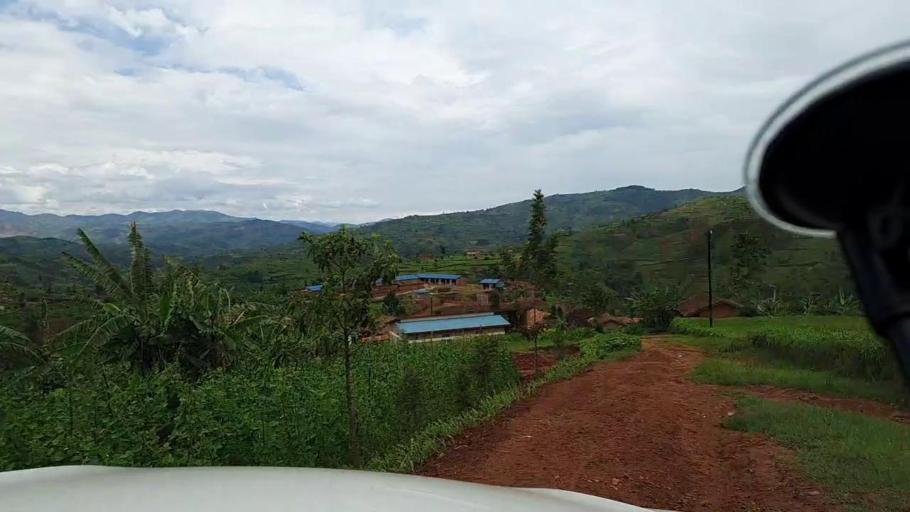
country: RW
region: Southern Province
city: Gitarama
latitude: -2.0664
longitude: 29.6462
